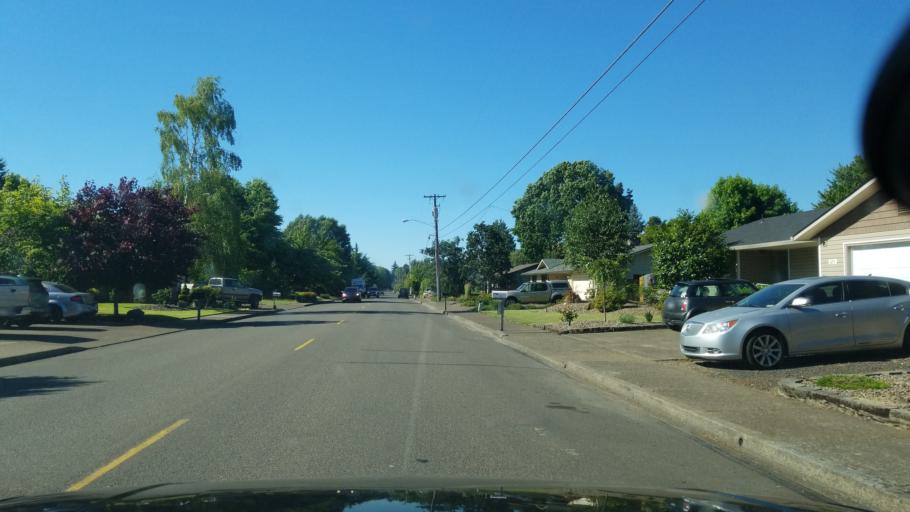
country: US
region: Oregon
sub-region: Yamhill County
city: McMinnville
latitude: 45.2253
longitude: -123.2076
